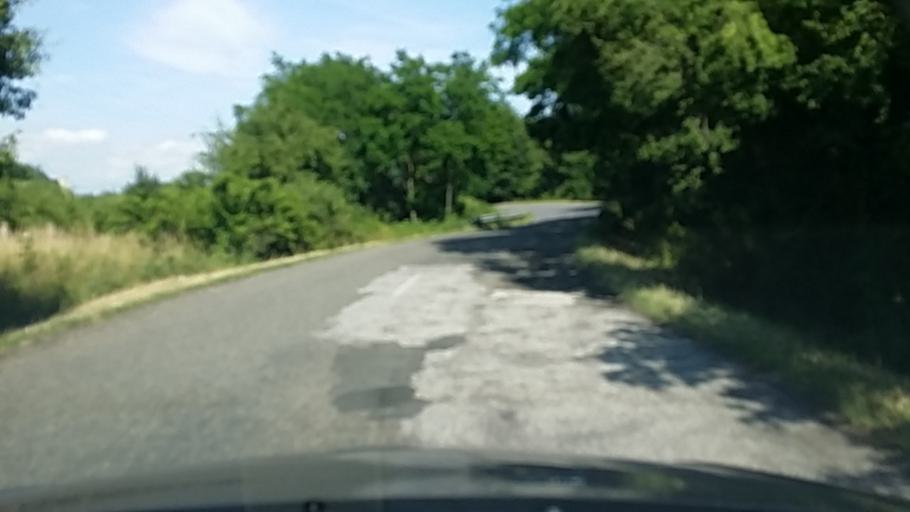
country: SK
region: Nitriansky
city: Sahy
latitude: 48.0578
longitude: 18.9560
